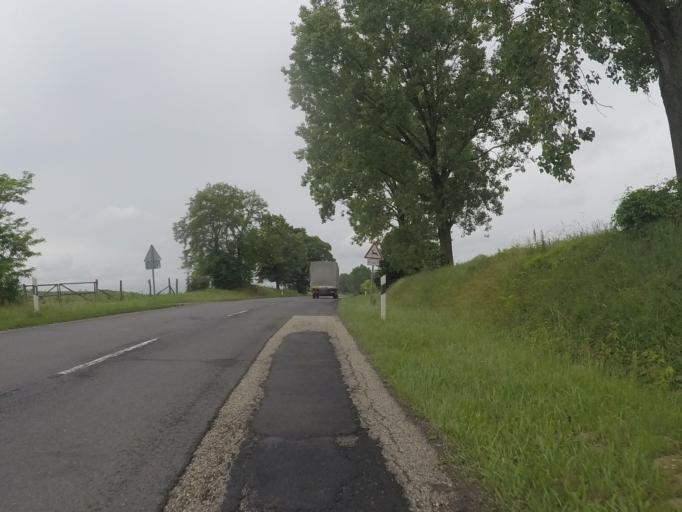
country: HU
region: Gyor-Moson-Sopron
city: Pannonhalma
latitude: 47.4931
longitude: 17.7799
